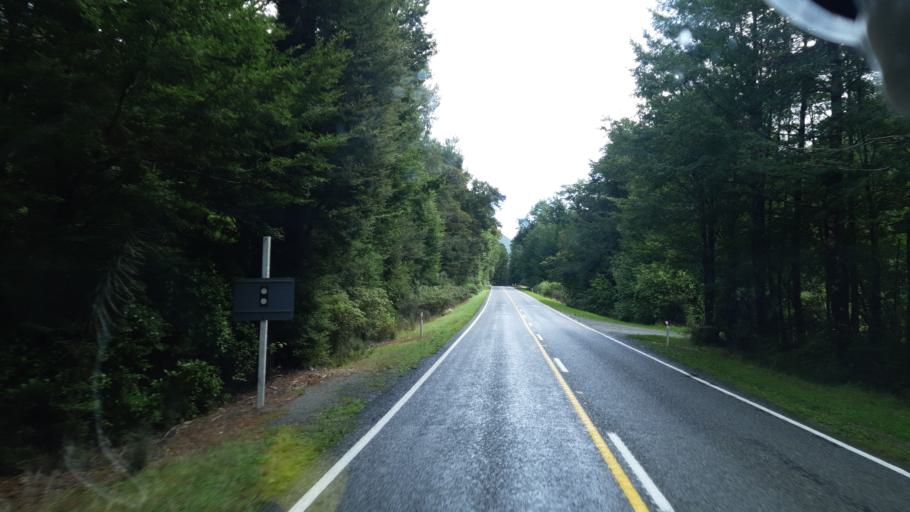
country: NZ
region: Canterbury
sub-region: Hurunui District
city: Amberley
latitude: -42.3806
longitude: 172.3158
